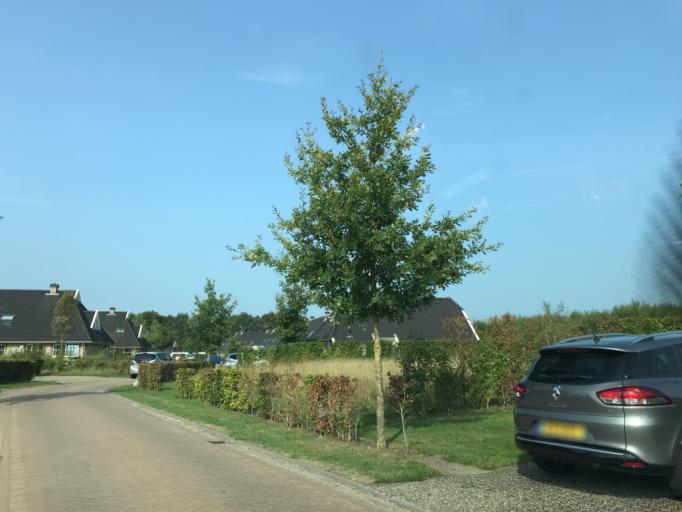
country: NL
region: Drenthe
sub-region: Gemeente Coevorden
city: Sleen
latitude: 52.8344
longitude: 6.6593
